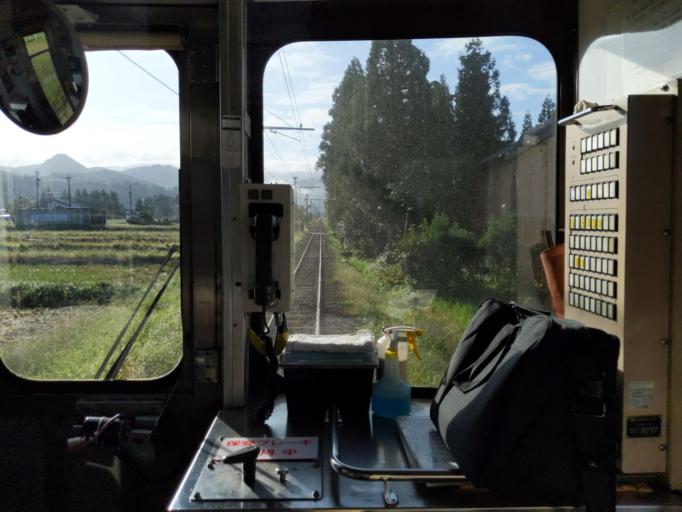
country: JP
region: Toyama
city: Kamiichi
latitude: 36.5939
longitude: 137.3263
